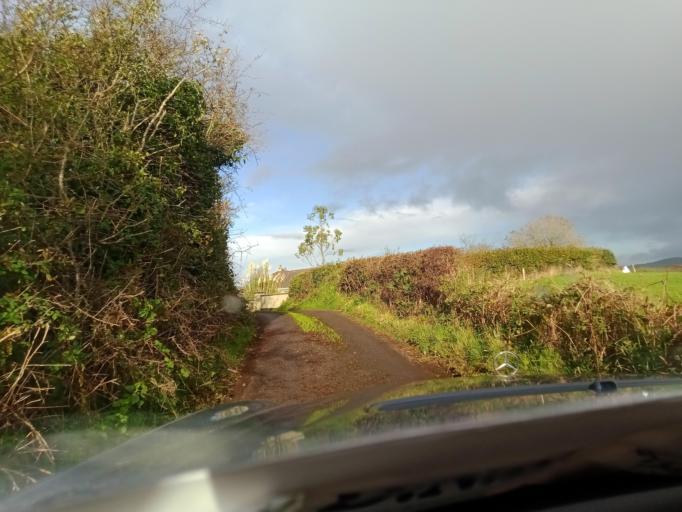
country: IE
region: Leinster
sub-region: Kilkenny
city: Mooncoin
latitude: 52.2983
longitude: -7.2718
